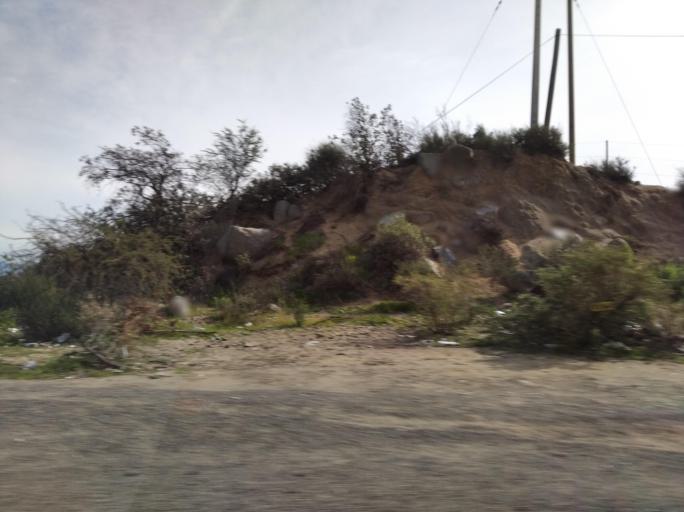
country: CL
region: Valparaiso
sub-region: Provincia de San Felipe
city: Llaillay
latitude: -33.0670
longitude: -71.0195
